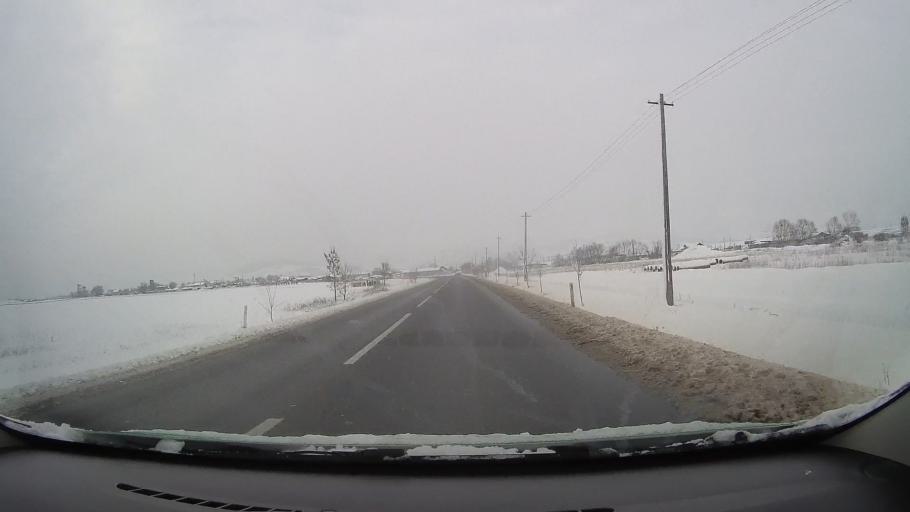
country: RO
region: Alba
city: Vurpar
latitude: 45.9865
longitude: 23.5094
